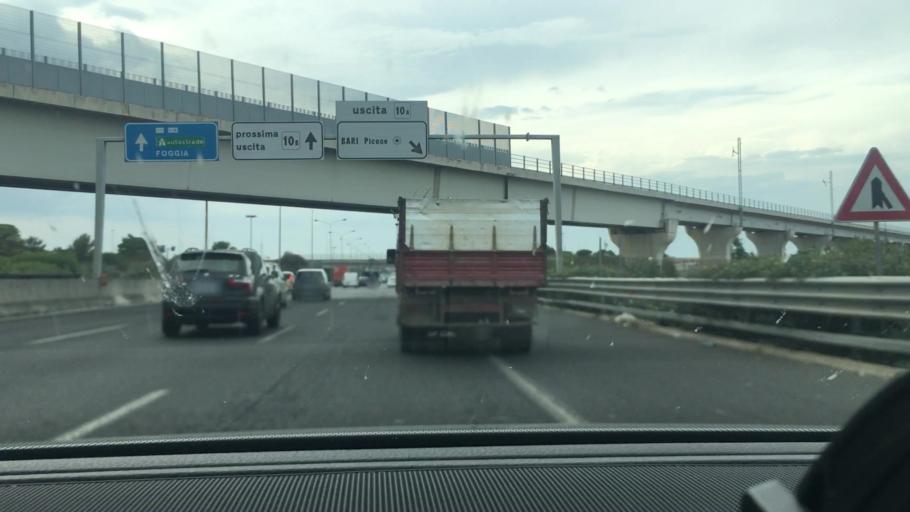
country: IT
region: Apulia
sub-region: Provincia di Bari
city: Bari
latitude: 41.0928
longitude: 16.8439
